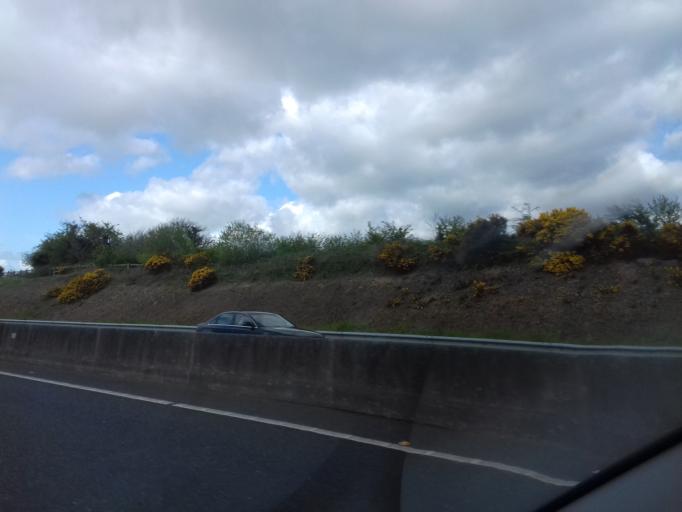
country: IE
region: Leinster
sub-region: Kilkenny
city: Thomastown
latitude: 52.4515
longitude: -7.2364
